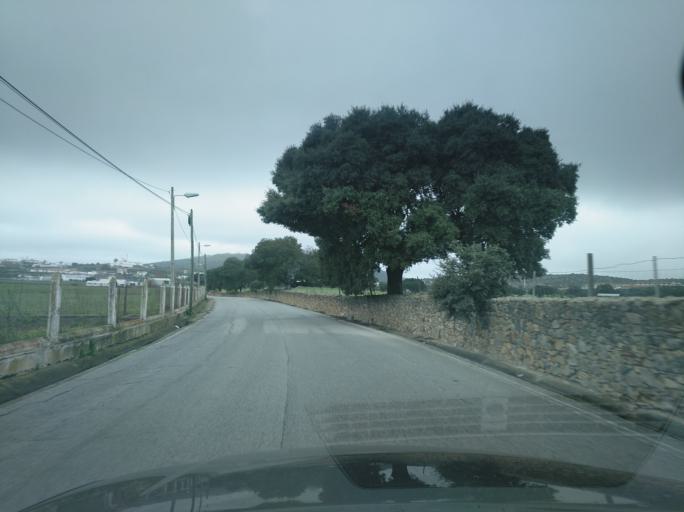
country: PT
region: Portalegre
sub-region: Elvas
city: Elvas
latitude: 38.8891
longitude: -7.1331
